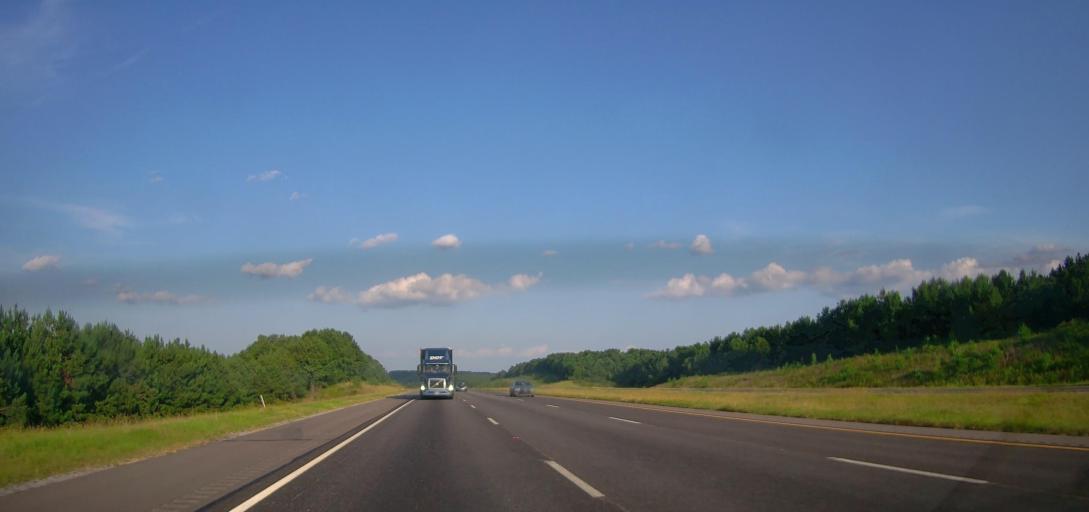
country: US
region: Alabama
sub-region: Walker County
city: Dora
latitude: 33.6915
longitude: -87.1190
